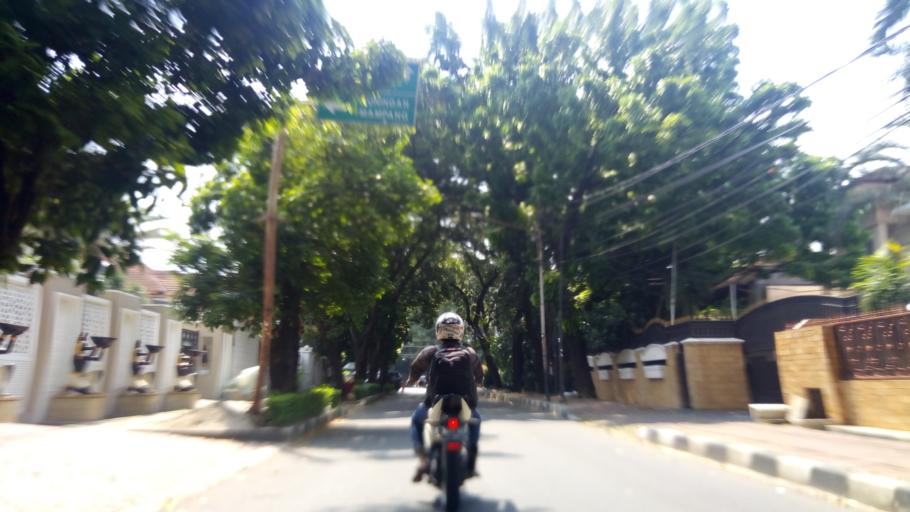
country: ID
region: Jakarta Raya
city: Jakarta
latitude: -6.2021
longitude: 106.8308
